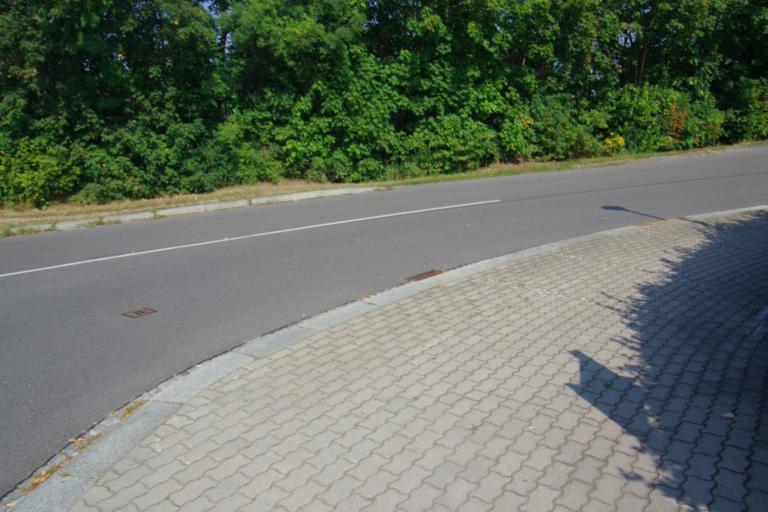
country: DE
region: Saxony
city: Frankenberg
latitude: 50.9095
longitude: 13.0419
